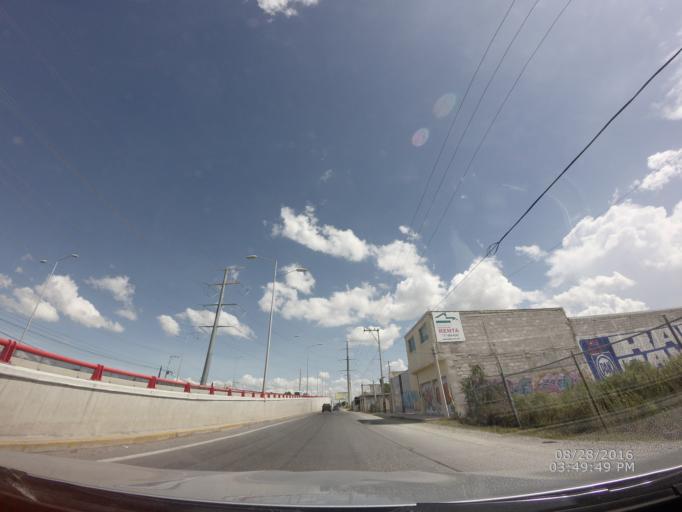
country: MX
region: Hidalgo
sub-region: Mineral de la Reforma
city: Rinconada de los Angeles
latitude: 20.0399
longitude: -98.7331
